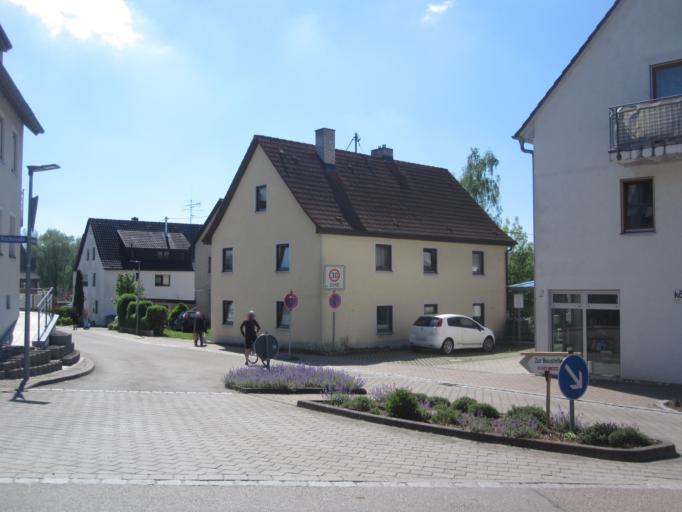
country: DE
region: Baden-Wuerttemberg
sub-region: Tuebingen Region
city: Westerstetten
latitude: 48.5193
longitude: 9.9547
